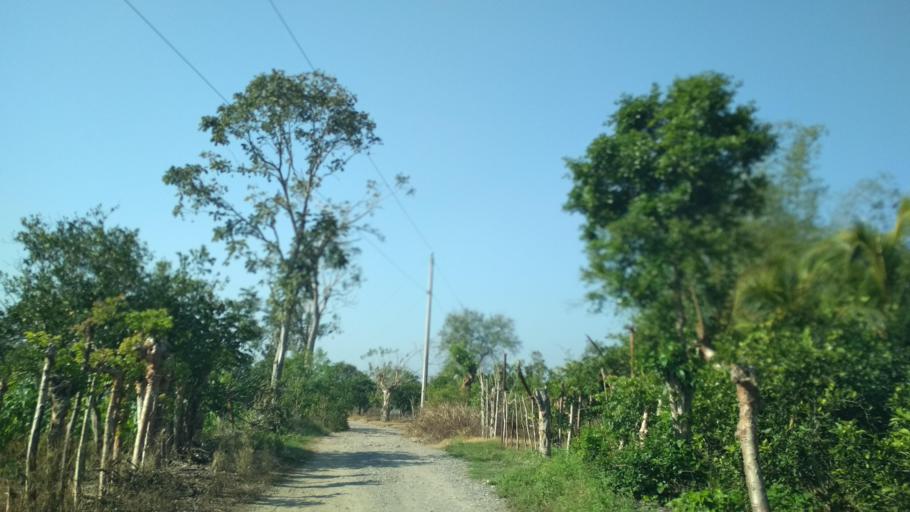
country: MX
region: Veracruz
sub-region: Papantla
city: Polutla
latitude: 20.4580
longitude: -97.2082
